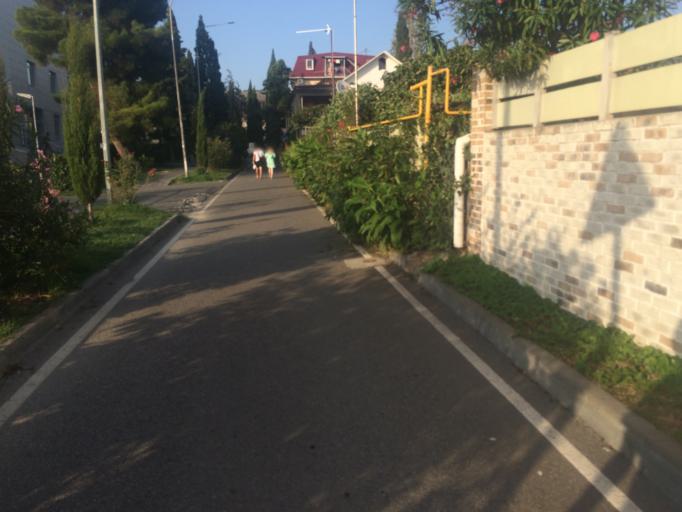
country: RU
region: Krasnodarskiy
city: Adler
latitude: 43.3888
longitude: 39.9864
